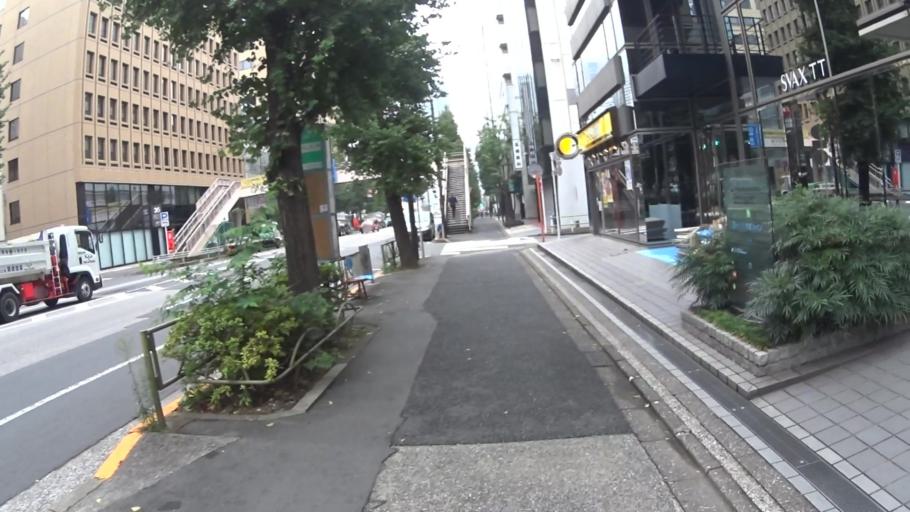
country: JP
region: Tokyo
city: Tokyo
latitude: 35.6652
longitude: 139.7469
